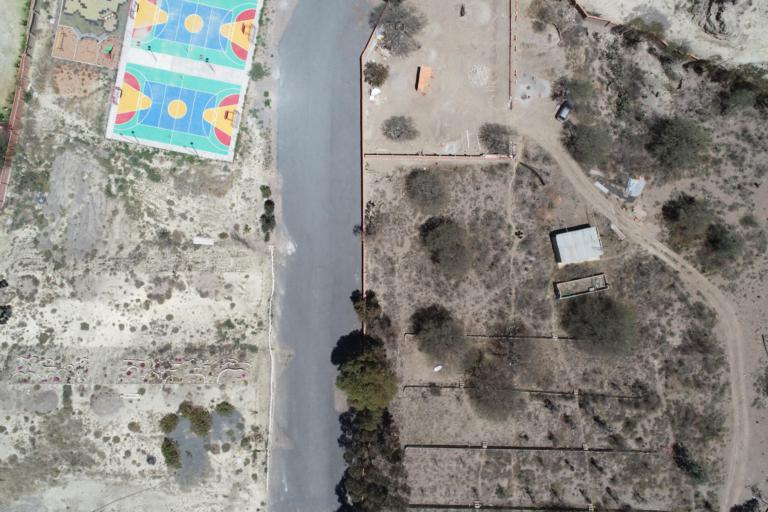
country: BO
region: La Paz
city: La Paz
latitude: -16.6202
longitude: -68.0581
